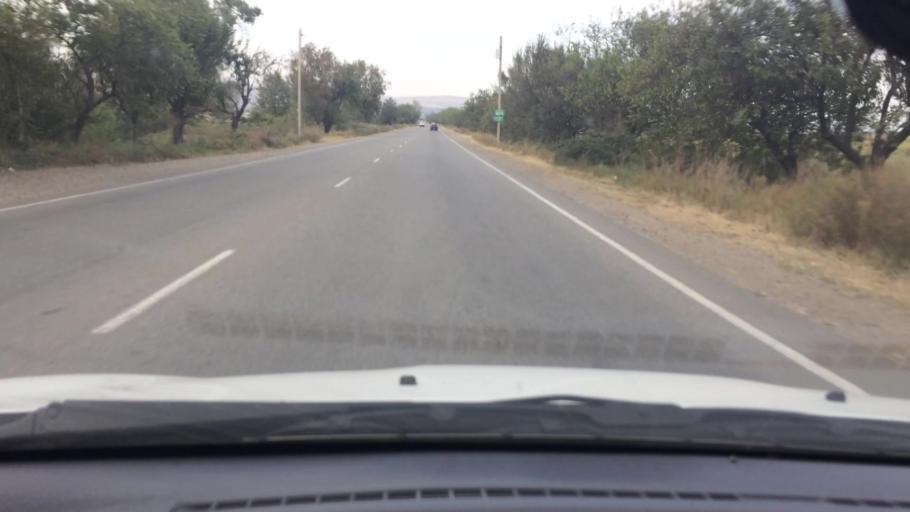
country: GE
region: Kvemo Kartli
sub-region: Marneuli
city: Marneuli
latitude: 41.5611
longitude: 44.7758
